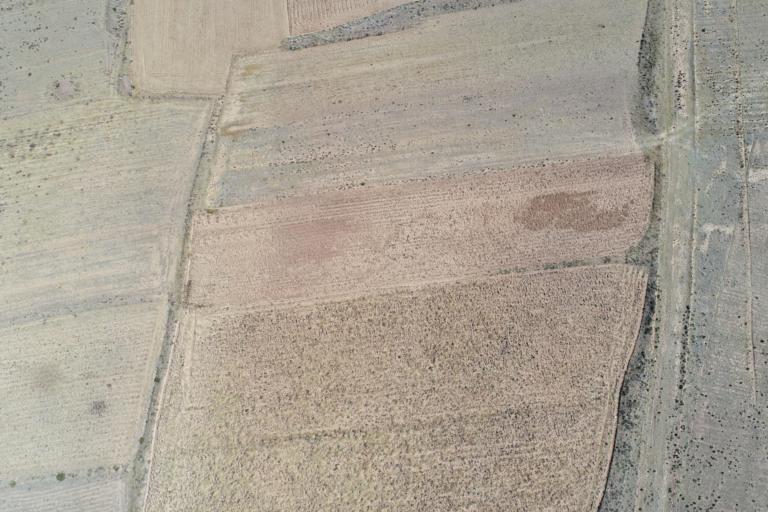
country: BO
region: La Paz
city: Achacachi
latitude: -15.9035
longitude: -68.8990
